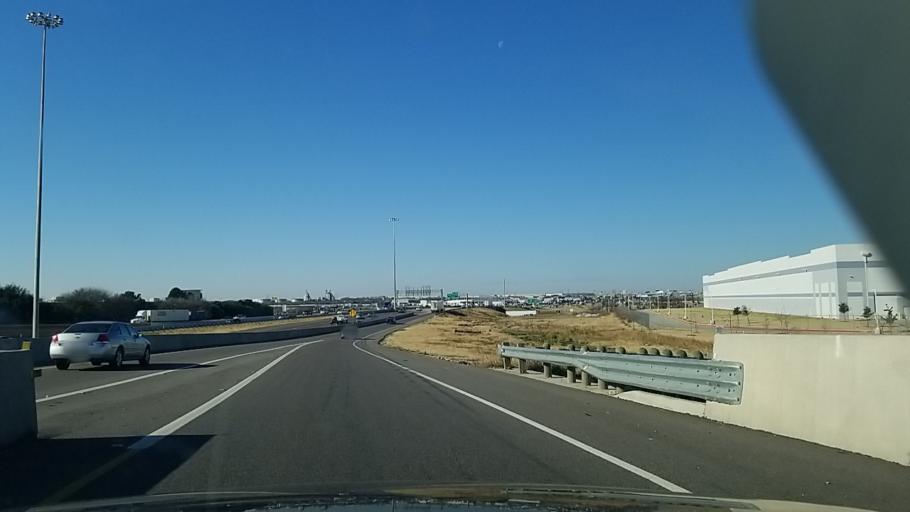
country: US
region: Texas
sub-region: Tarrant County
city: Blue Mound
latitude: 32.8404
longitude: -97.3166
